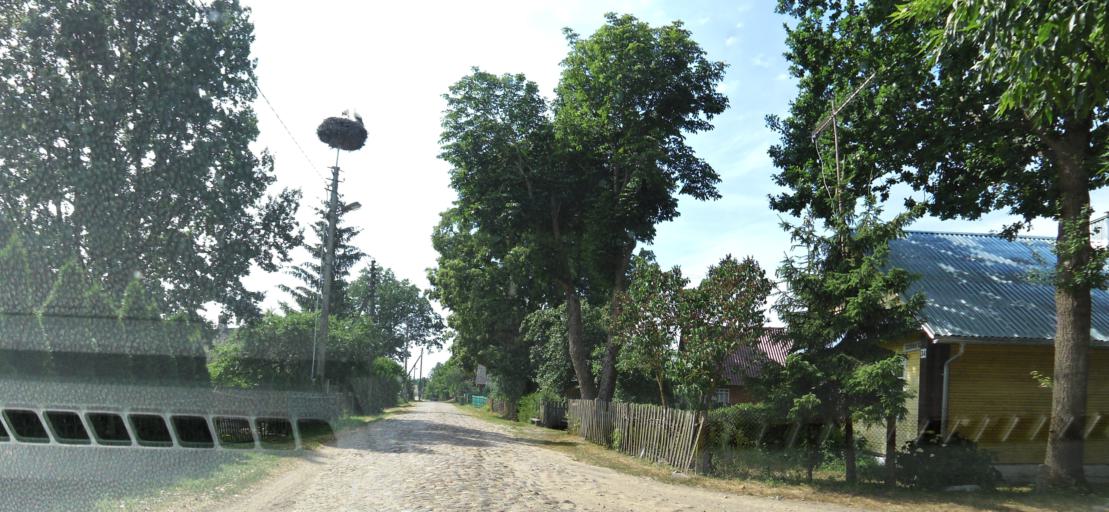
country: LT
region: Vilnius County
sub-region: Trakai
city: Rudiskes
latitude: 54.3671
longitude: 24.8463
